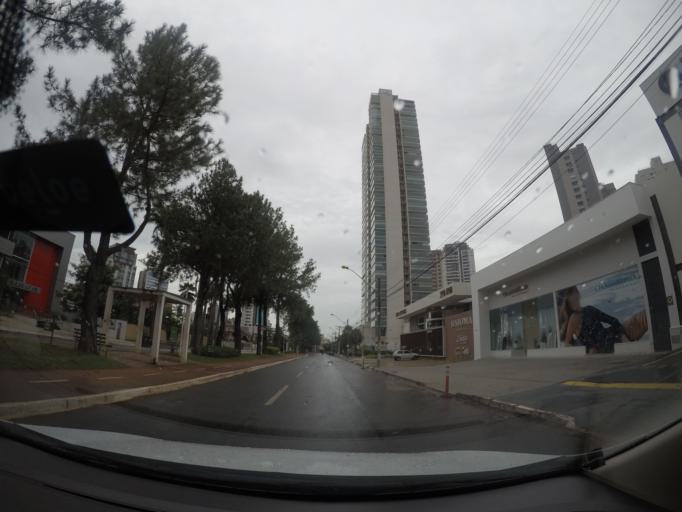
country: BR
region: Goias
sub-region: Goiania
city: Goiania
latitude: -16.7002
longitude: -49.2560
